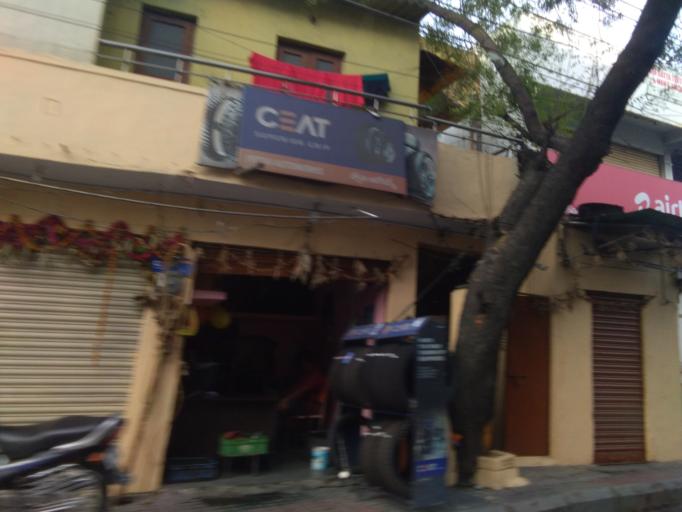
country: IN
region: Telangana
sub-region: Rangareddi
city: Quthbullapur
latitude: 17.4604
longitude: 78.4757
